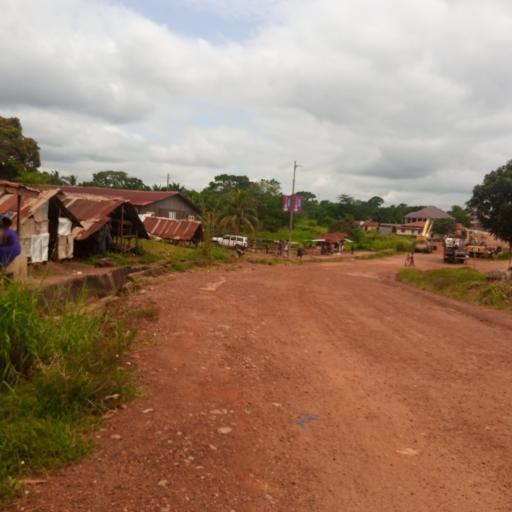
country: SL
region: Eastern Province
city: Kenema
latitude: 7.8589
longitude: -11.2034
